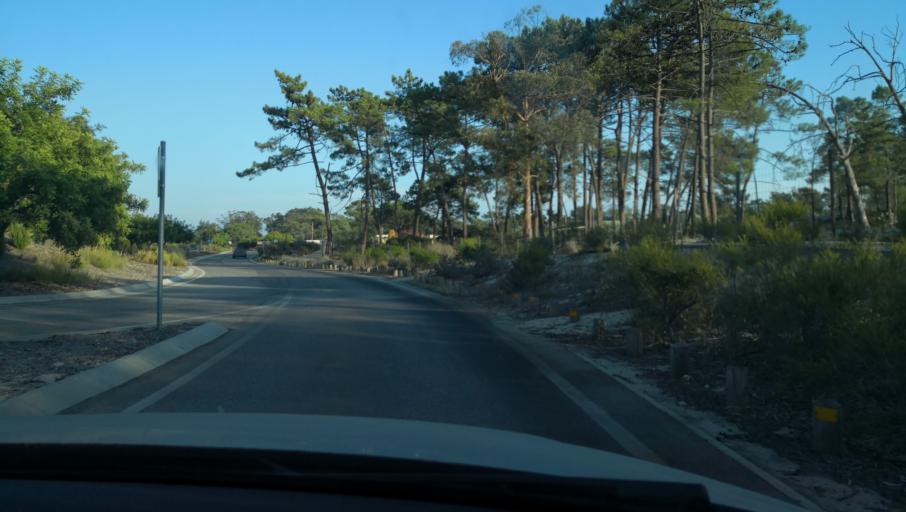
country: PT
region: Setubal
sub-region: Setubal
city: Setubal
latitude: 38.4663
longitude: -8.8752
